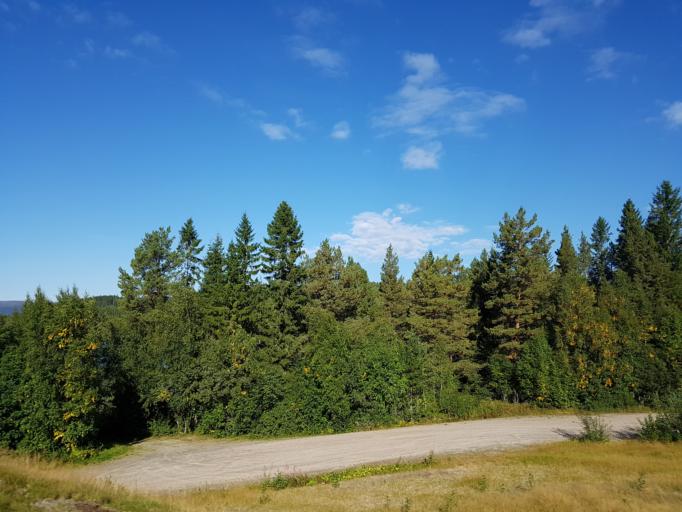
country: NO
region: Sor-Trondelag
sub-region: Trondheim
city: Trondheim
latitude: 63.6312
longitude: 10.2615
